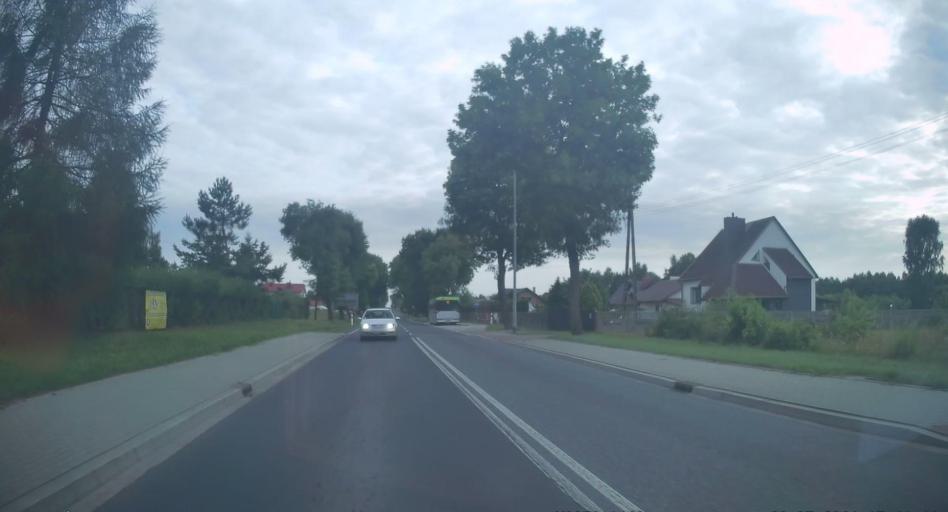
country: PL
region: Lodz Voivodeship
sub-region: Powiat radomszczanski
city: Radomsko
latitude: 51.1064
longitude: 19.4652
